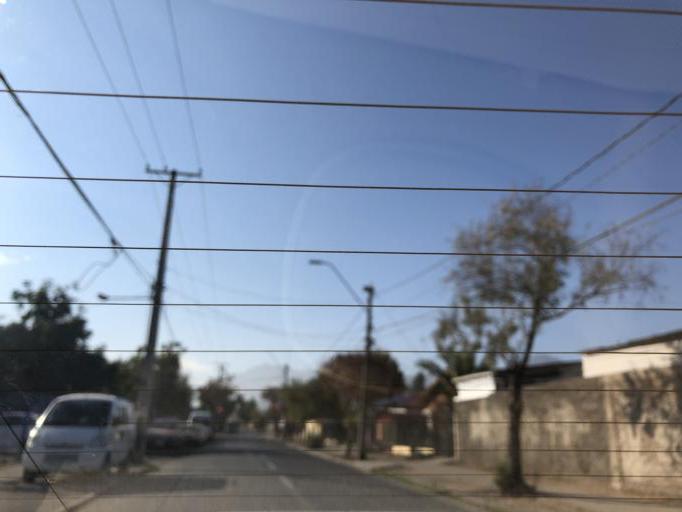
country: CL
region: Santiago Metropolitan
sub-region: Provincia de Cordillera
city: Puente Alto
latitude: -33.6238
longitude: -70.5887
